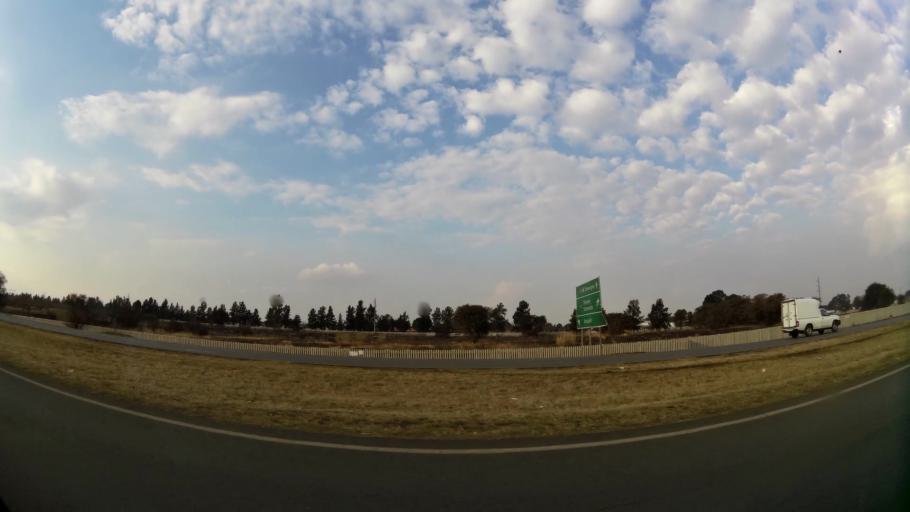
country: ZA
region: Gauteng
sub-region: Sedibeng District Municipality
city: Vereeniging
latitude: -26.6484
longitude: 27.8767
